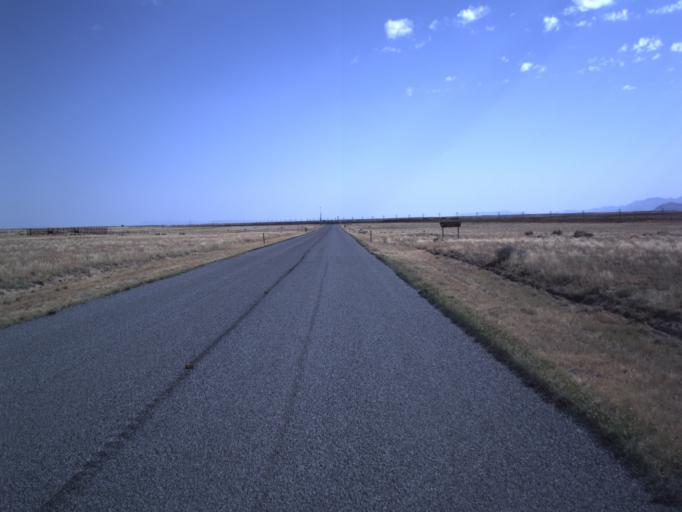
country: US
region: Utah
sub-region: Millard County
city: Fillmore
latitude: 38.9110
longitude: -112.8165
